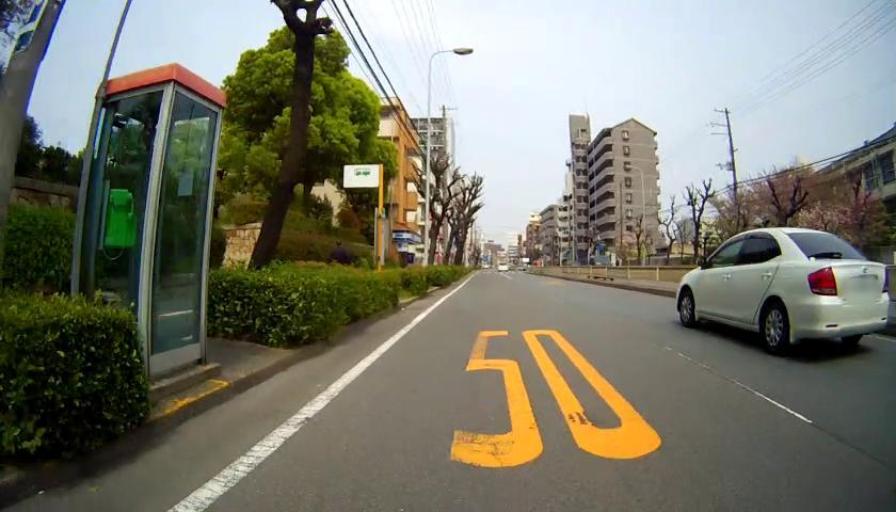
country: JP
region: Osaka
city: Suita
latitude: 34.7441
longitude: 135.5373
